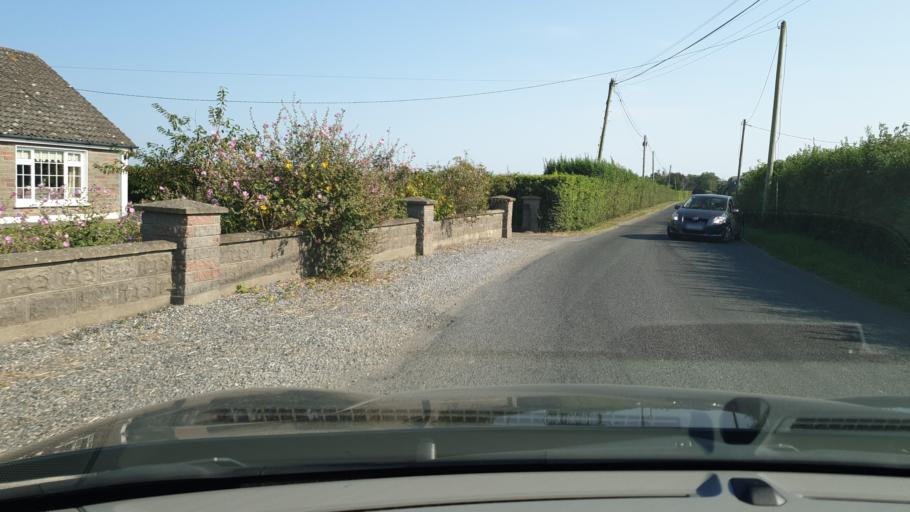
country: IE
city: Kentstown
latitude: 53.6126
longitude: -6.5057
